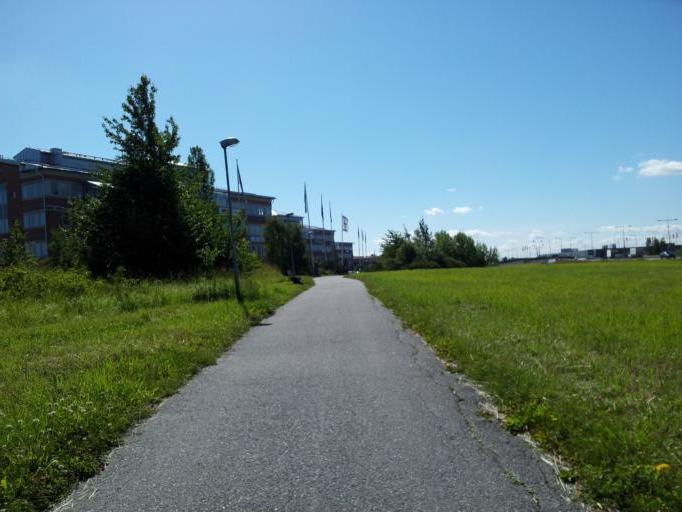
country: SE
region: Uppsala
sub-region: Uppsala Kommun
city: Saevja
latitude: 59.8568
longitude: 17.6828
